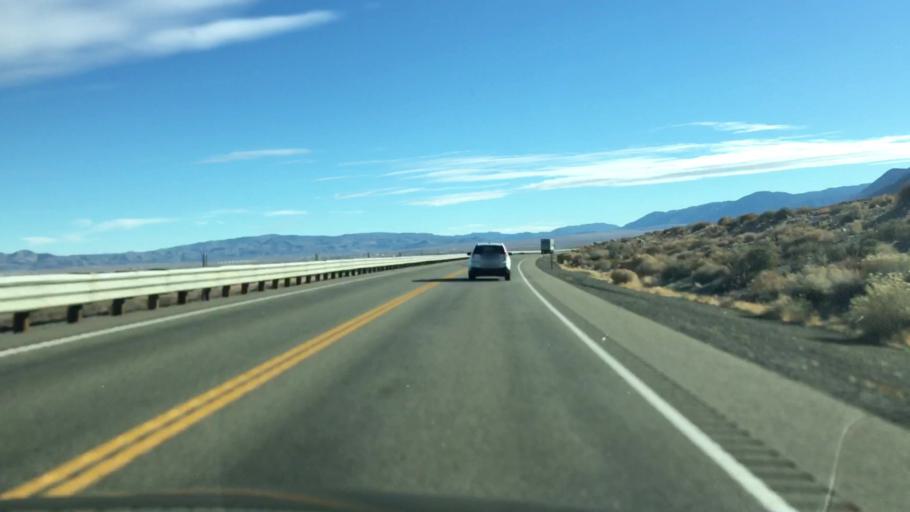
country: US
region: Nevada
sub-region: Mineral County
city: Hawthorne
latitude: 38.6071
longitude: -118.7132
